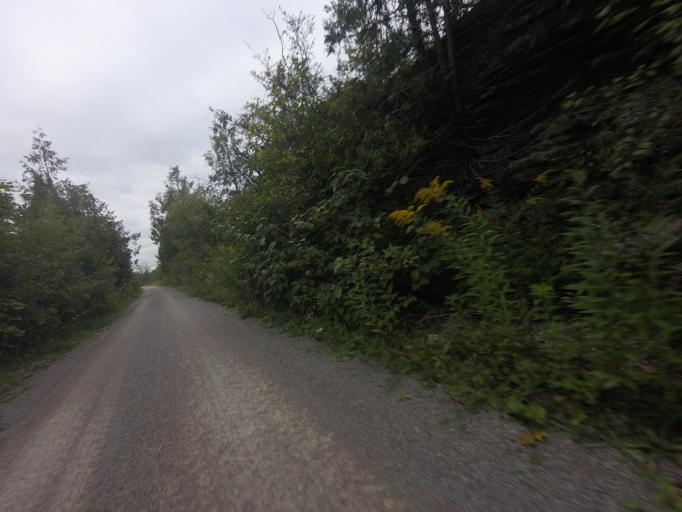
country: CA
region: Ontario
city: Omemee
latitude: 44.5225
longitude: -78.7330
